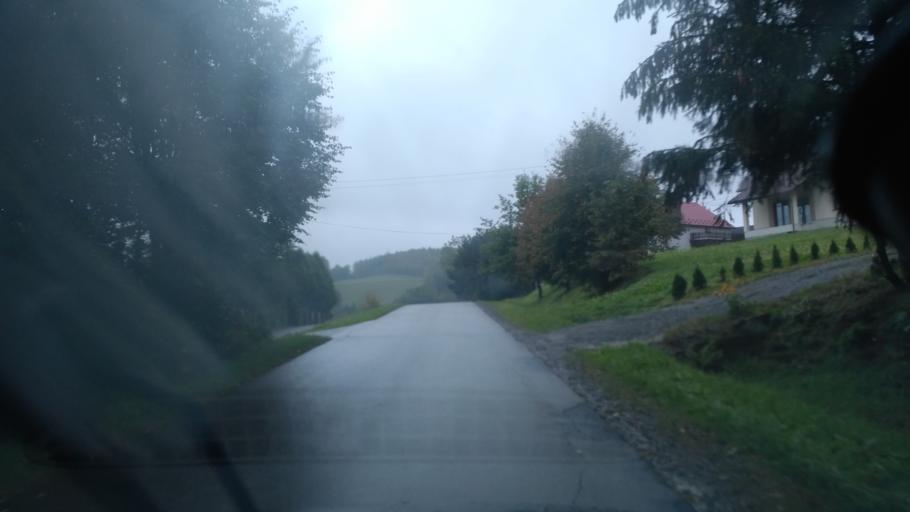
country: PL
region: Subcarpathian Voivodeship
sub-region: Powiat ropczycko-sedziszowski
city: Niedzwiada
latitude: 50.0293
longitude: 21.5440
